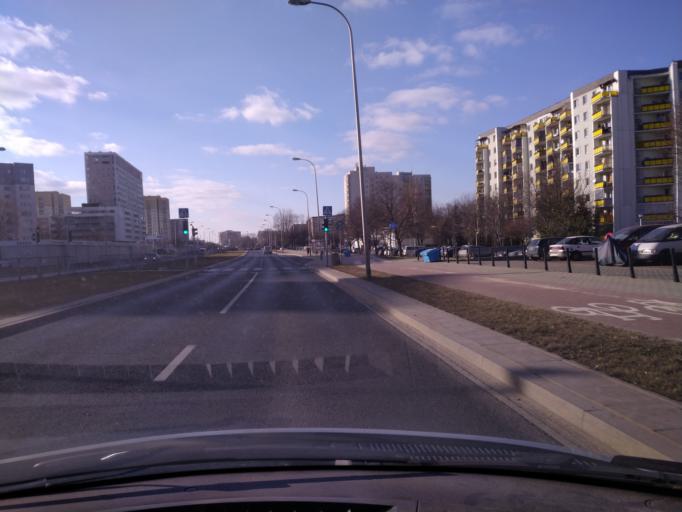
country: PL
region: Masovian Voivodeship
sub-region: Warszawa
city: Praga Poludnie
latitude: 52.2240
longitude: 21.0981
